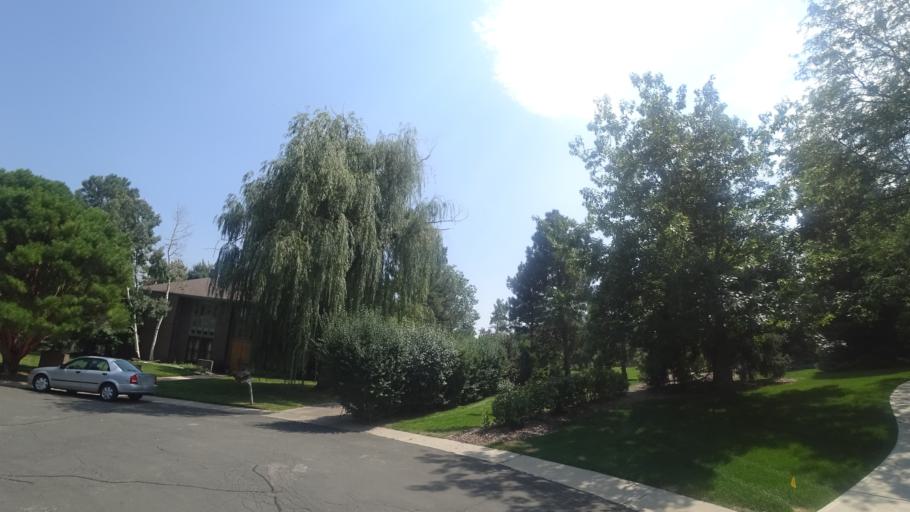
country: US
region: Colorado
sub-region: Arapahoe County
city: Greenwood Village
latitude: 39.6192
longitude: -104.9667
